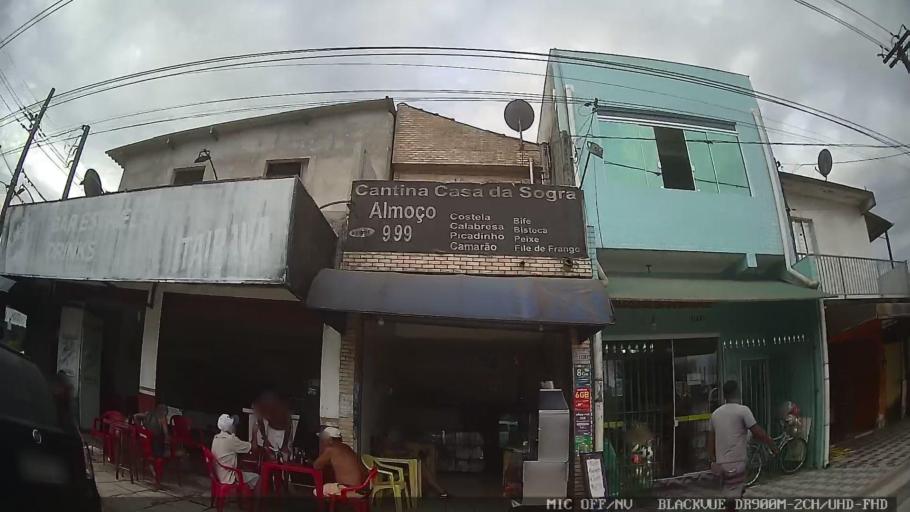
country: BR
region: Sao Paulo
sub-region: Bertioga
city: Bertioga
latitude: -23.8058
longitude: -46.0543
